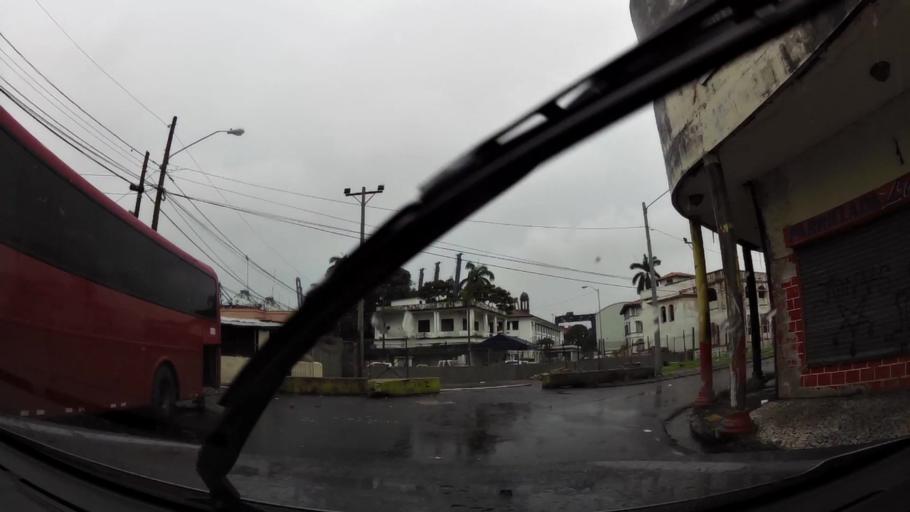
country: PA
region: Colon
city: Colon
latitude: 9.3533
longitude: -79.9034
